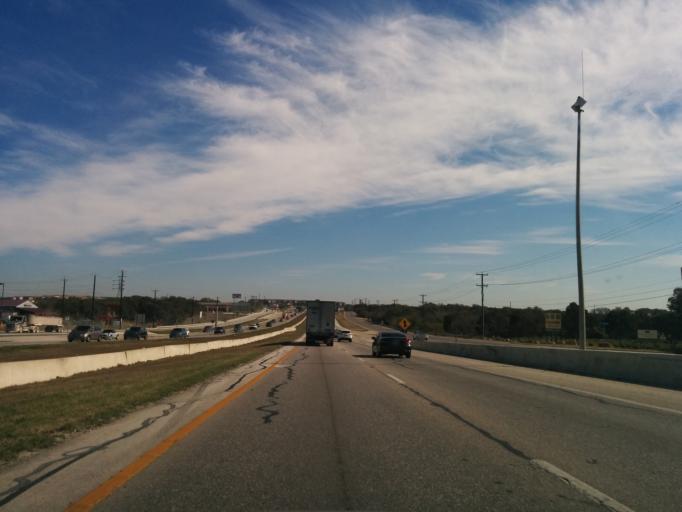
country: US
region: Texas
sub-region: Bexar County
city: Shavano Park
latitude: 29.5945
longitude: -98.5745
